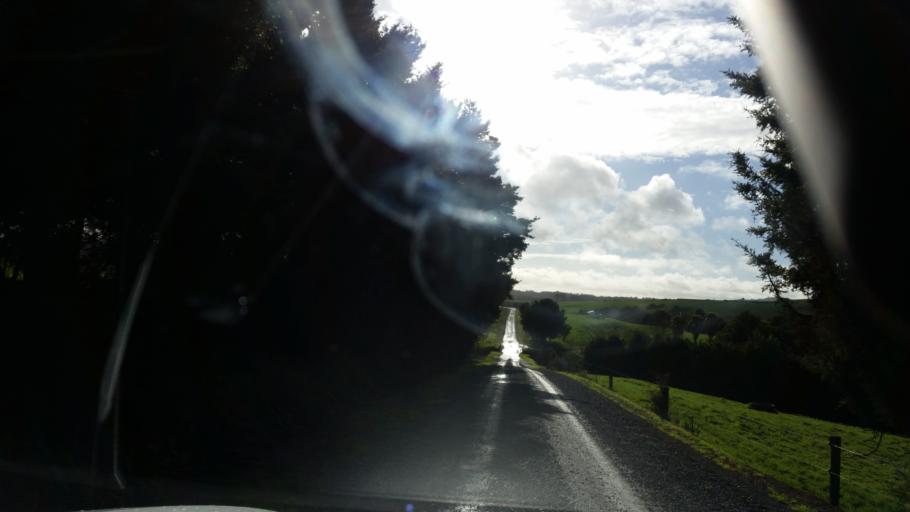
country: NZ
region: Northland
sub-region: Whangarei
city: Maungatapere
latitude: -35.6911
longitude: 174.1189
